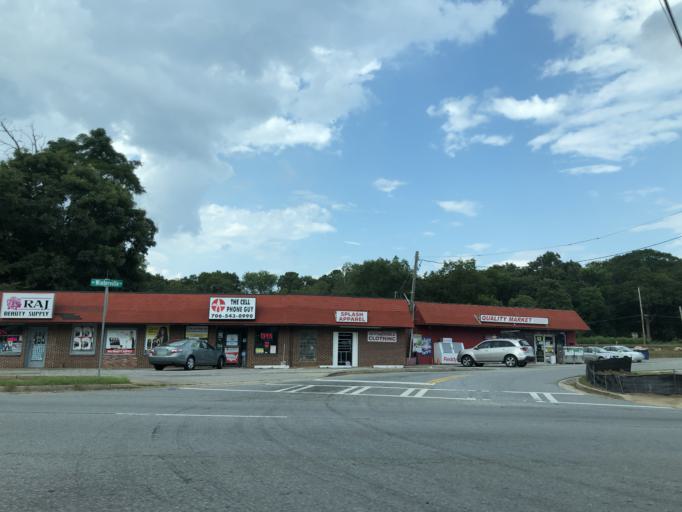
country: US
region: Georgia
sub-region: Clarke County
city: Athens
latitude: 33.9481
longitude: -83.3585
